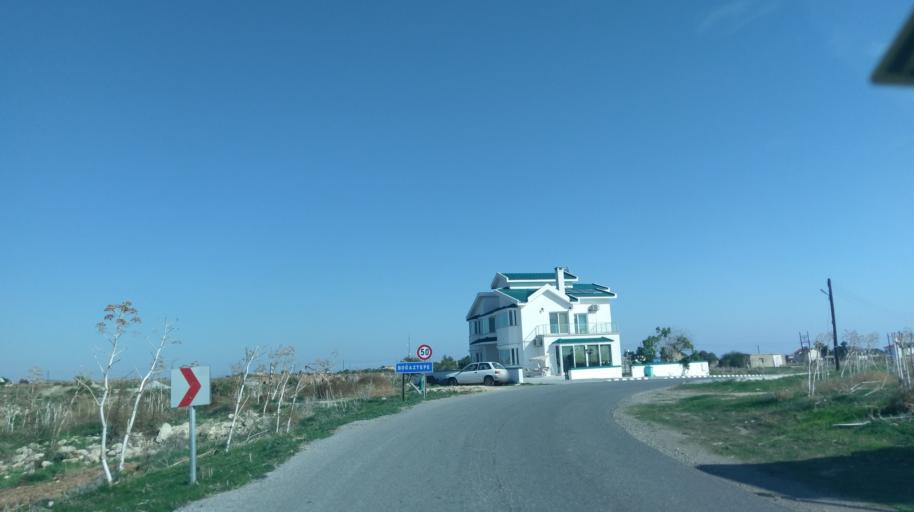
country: CY
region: Ammochostos
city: Trikomo
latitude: 35.3168
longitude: 33.9422
